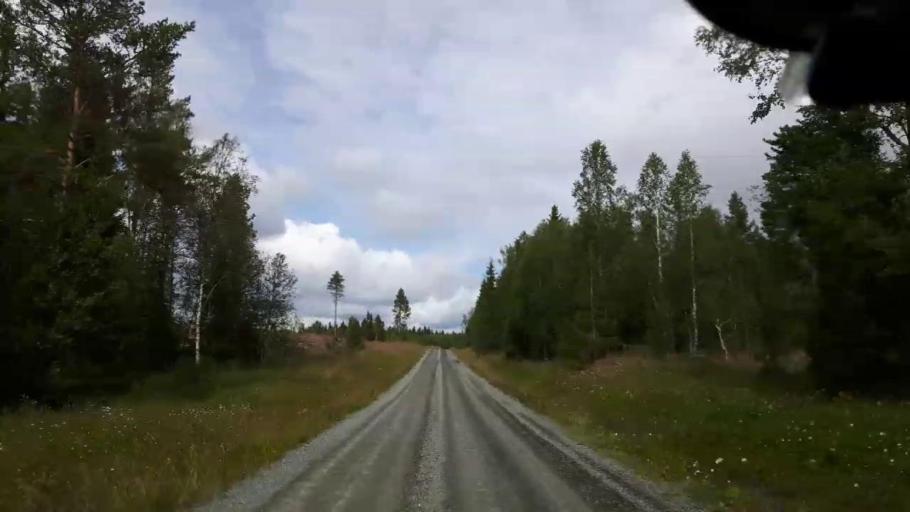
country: SE
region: Jaemtland
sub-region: Krokoms Kommun
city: Valla
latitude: 63.5502
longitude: 13.9168
